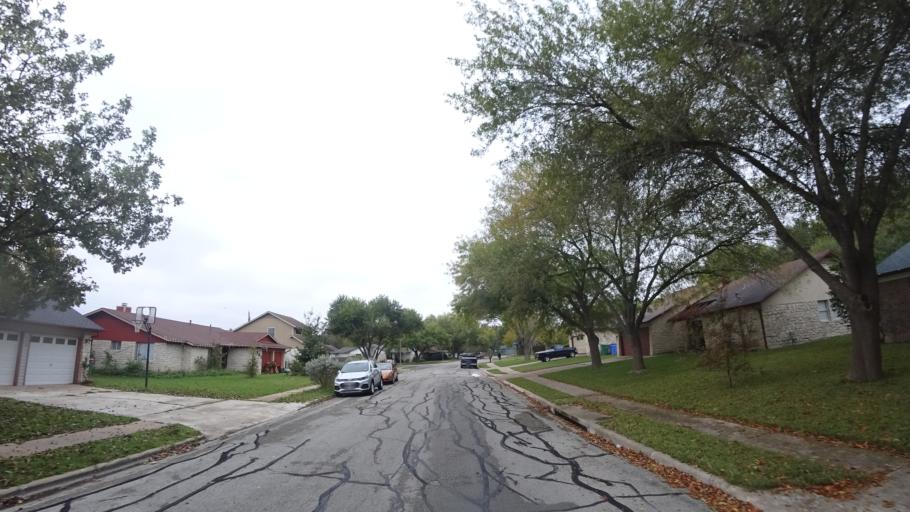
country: US
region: Texas
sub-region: Travis County
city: Pflugerville
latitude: 30.4257
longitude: -97.6084
